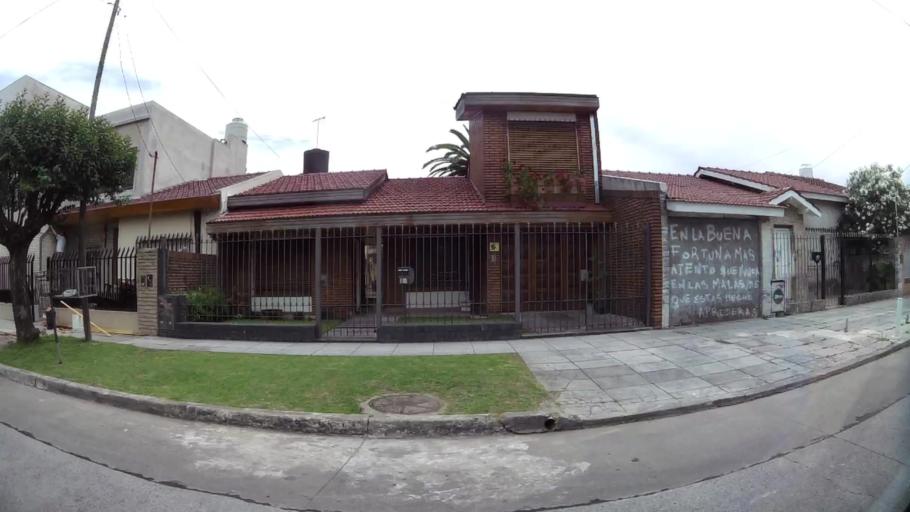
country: AR
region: Buenos Aires
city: San Justo
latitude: -34.6661
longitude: -58.5407
